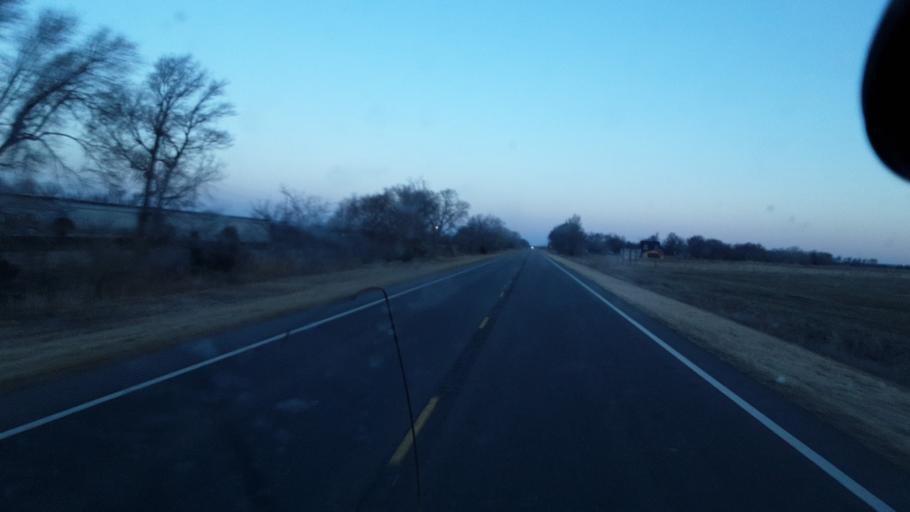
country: US
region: Kansas
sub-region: Reno County
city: Nickerson
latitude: 38.1087
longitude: -98.0271
